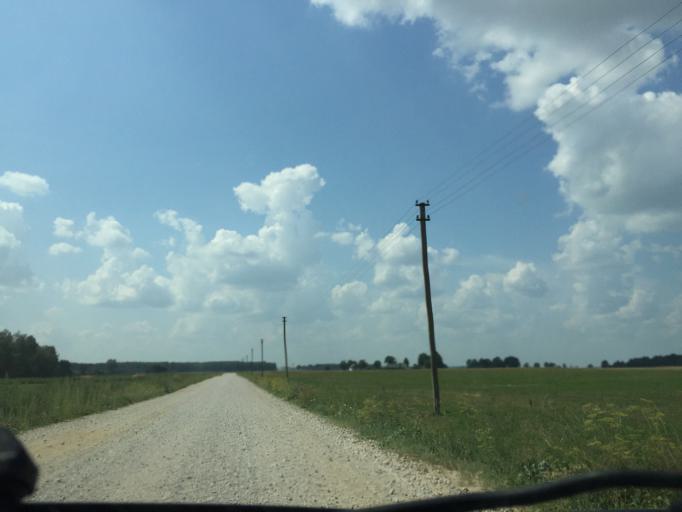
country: LT
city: Zagare
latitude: 56.4004
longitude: 23.2315
